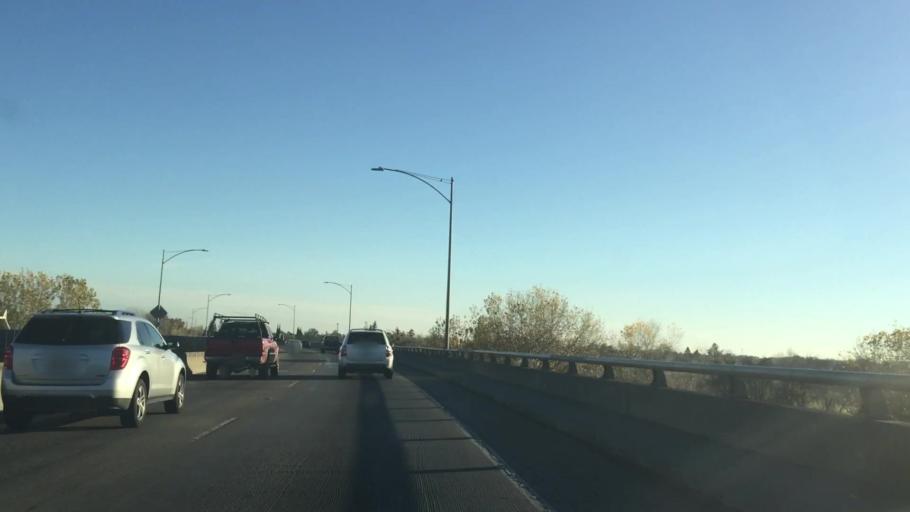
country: US
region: California
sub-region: Yuba County
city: Marysville
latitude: 39.1329
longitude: -121.5889
